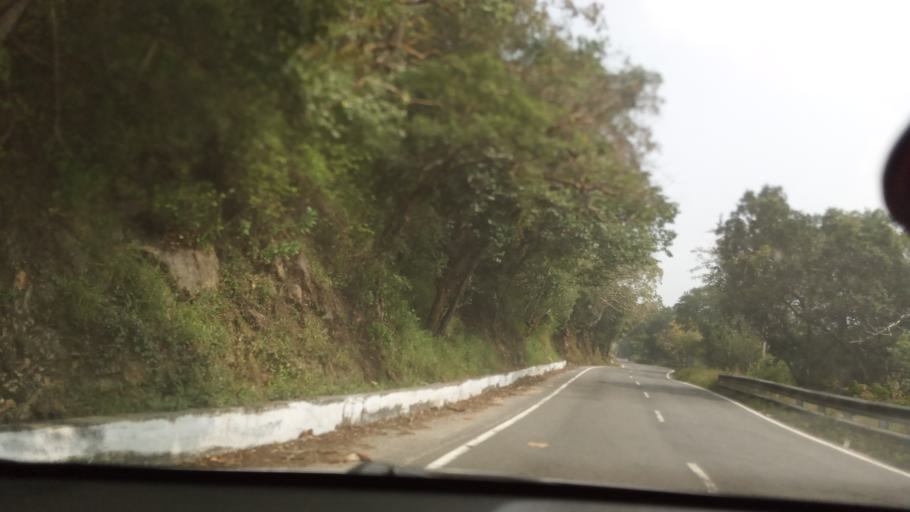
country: IN
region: Tamil Nadu
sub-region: Erode
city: Sathyamangalam
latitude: 11.6035
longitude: 77.1293
